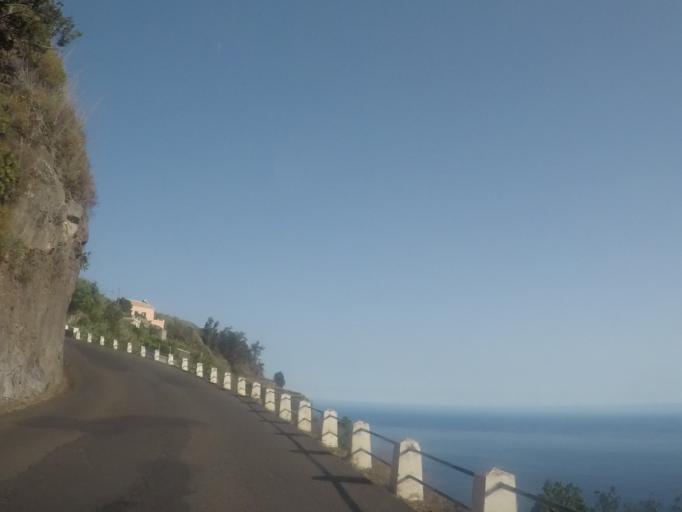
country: PT
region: Madeira
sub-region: Calheta
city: Arco da Calheta
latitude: 32.7074
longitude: -17.1304
